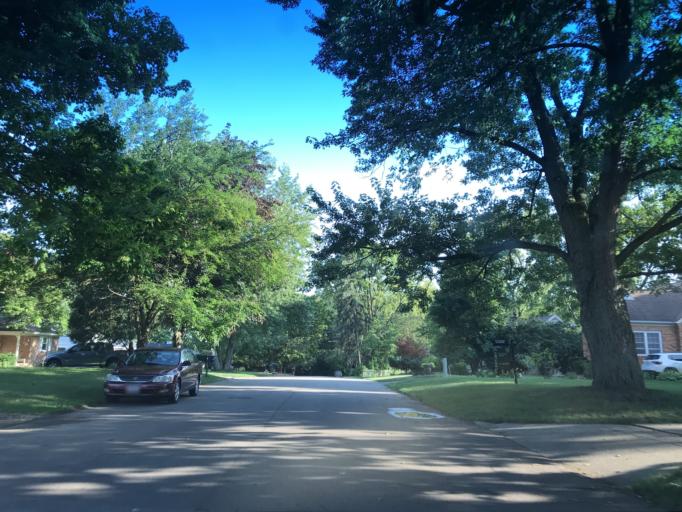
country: US
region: Michigan
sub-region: Eaton County
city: Waverly
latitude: 42.7081
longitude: -84.6088
